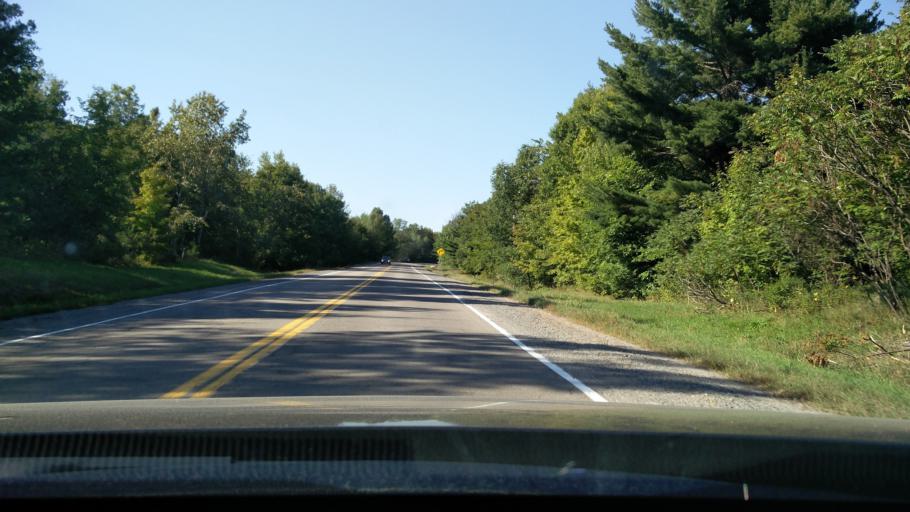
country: CA
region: Ontario
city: Perth
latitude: 44.7063
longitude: -76.4000
